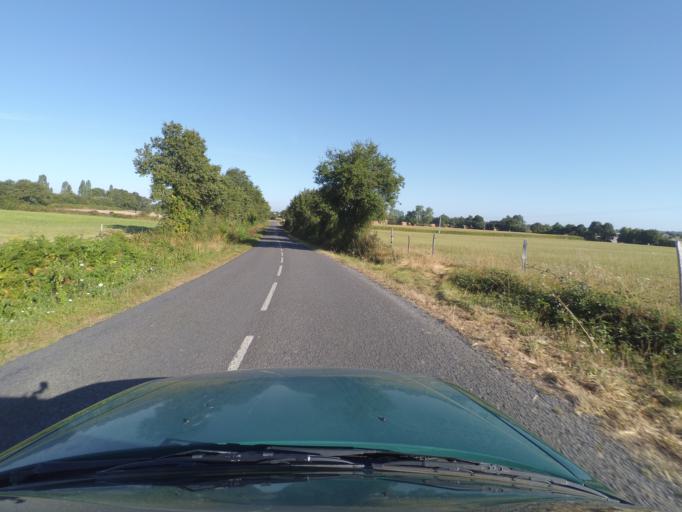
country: FR
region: Pays de la Loire
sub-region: Departement de la Loire-Atlantique
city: Le Bignon
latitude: 47.1022
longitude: -1.5032
